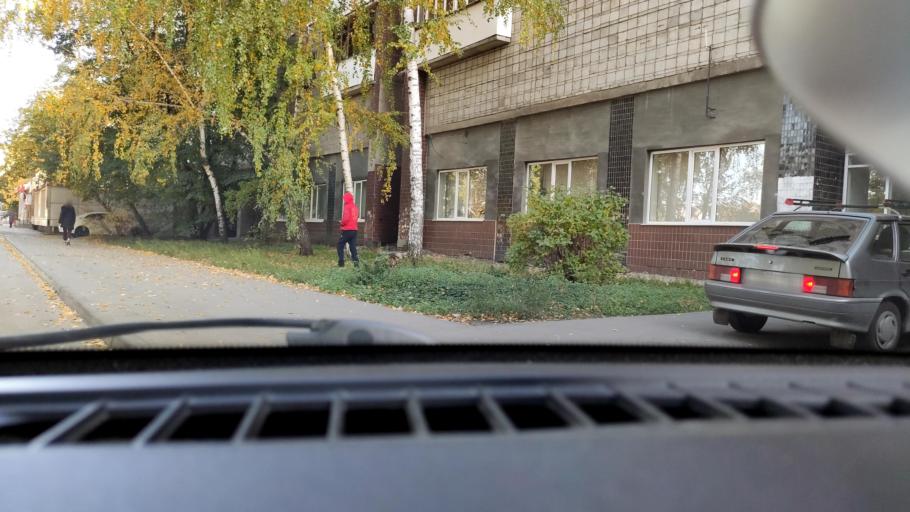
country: RU
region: Samara
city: Samara
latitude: 53.2059
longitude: 50.1349
